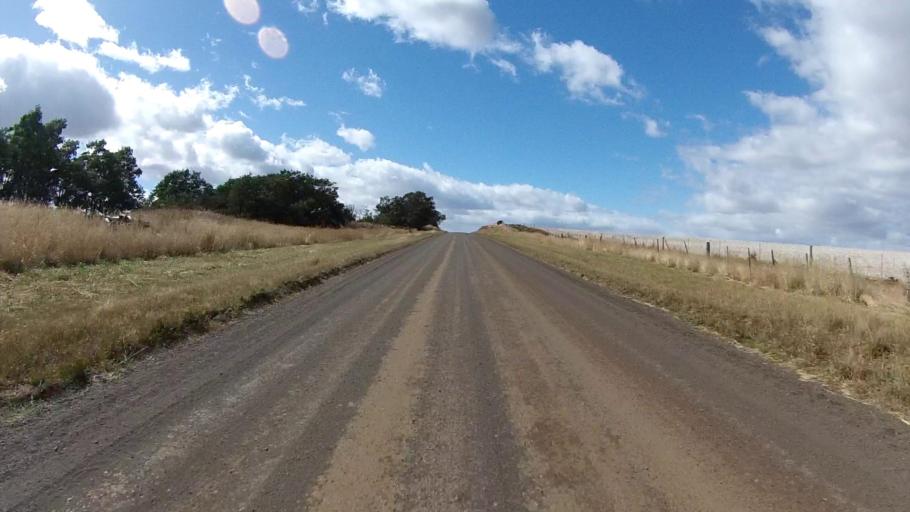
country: AU
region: Tasmania
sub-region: Northern Midlands
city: Evandale
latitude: -41.7110
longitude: 147.4099
